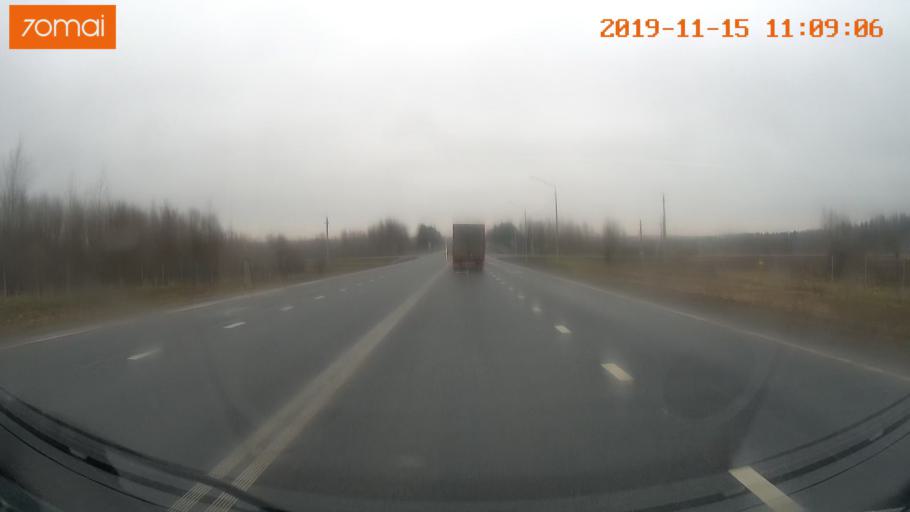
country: RU
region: Vologda
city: Chebsara
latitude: 59.1203
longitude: 39.0900
